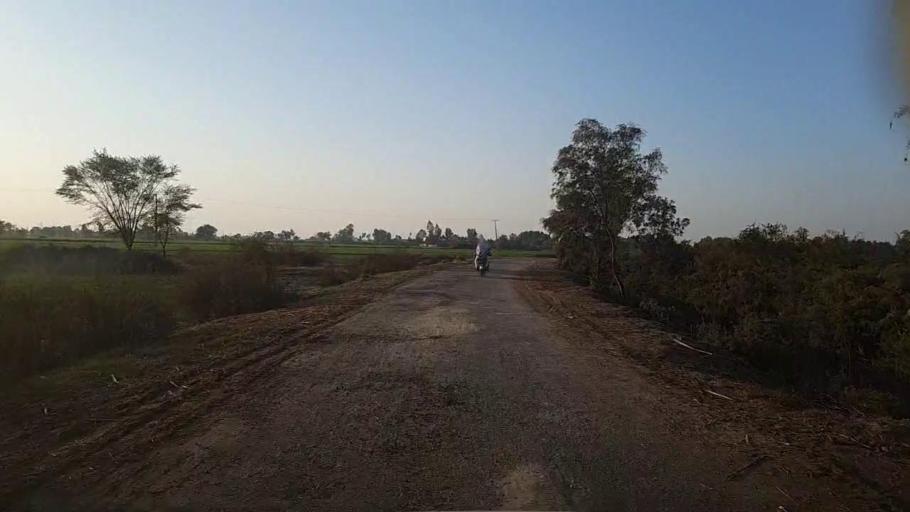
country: PK
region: Sindh
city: Mirpur Mathelo
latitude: 27.8768
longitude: 69.6500
